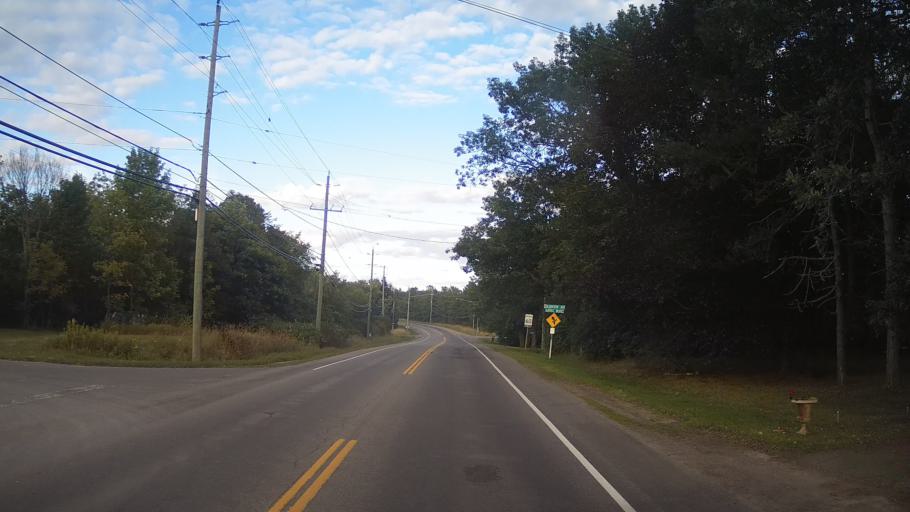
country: CA
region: Ontario
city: Kingston
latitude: 44.2431
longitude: -76.4259
